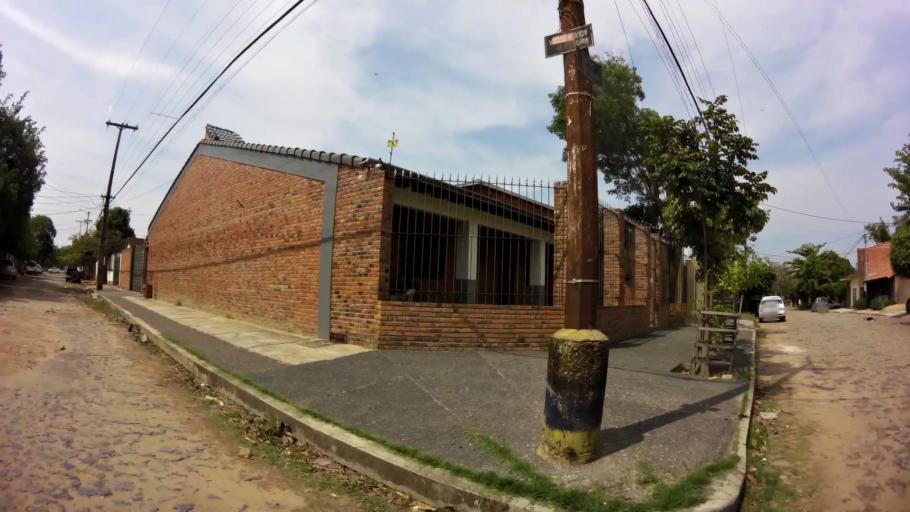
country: PY
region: Asuncion
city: Asuncion
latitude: -25.2603
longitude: -57.5856
